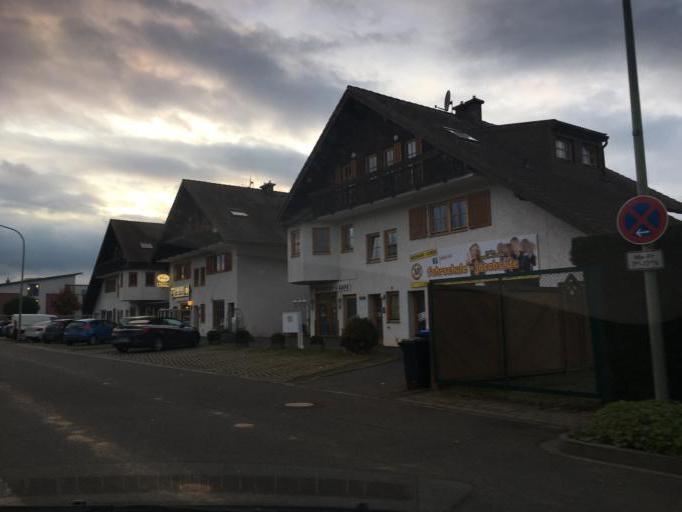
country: DE
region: North Rhine-Westphalia
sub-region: Regierungsbezirk Koln
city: Vettweiss
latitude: 50.7356
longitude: 6.5941
